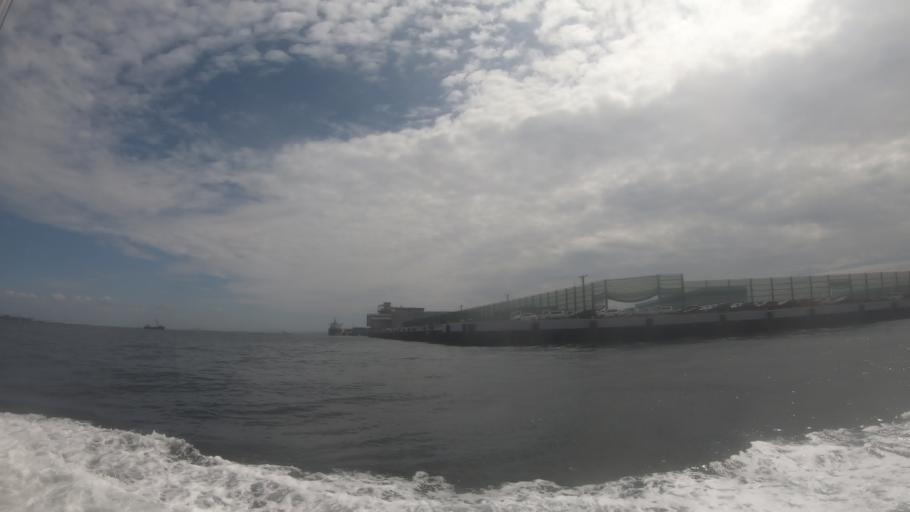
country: JP
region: Kanagawa
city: Yokohama
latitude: 35.3910
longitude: 139.6452
